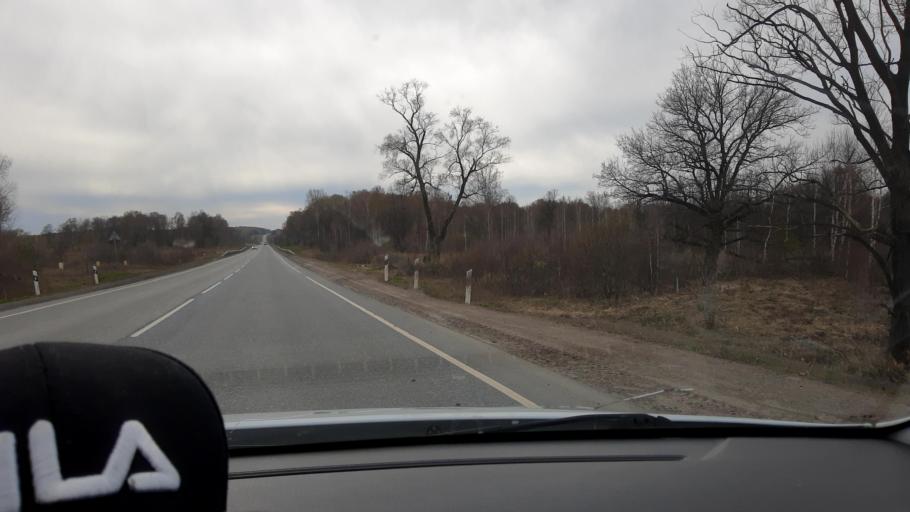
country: RU
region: Bashkortostan
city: Iglino
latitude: 54.7795
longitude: 56.5029
